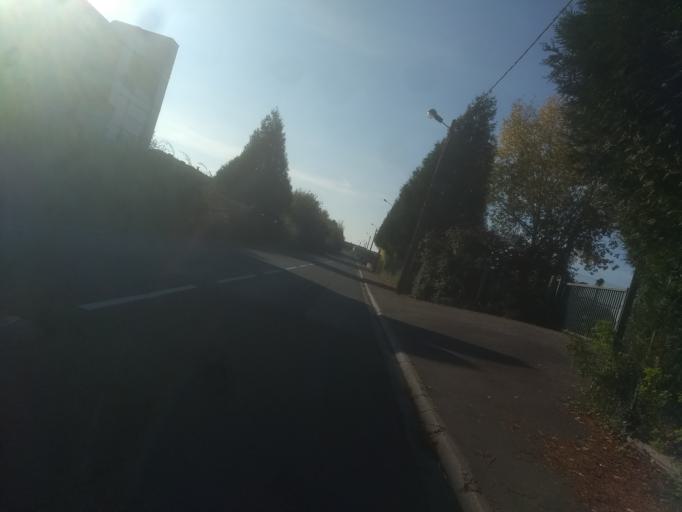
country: FR
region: Nord-Pas-de-Calais
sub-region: Departement du Pas-de-Calais
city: Achicourt
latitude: 50.2786
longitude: 2.7708
